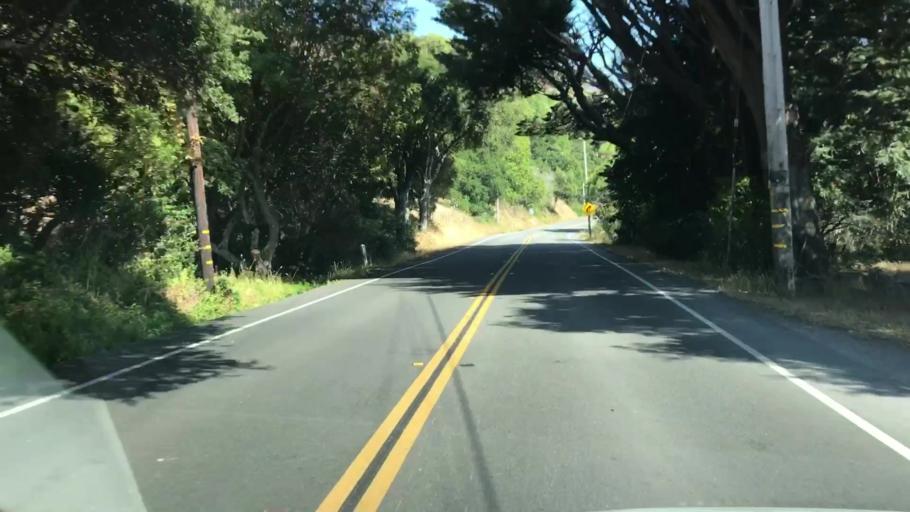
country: US
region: California
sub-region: Marin County
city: Lagunitas-Forest Knolls
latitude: 38.0439
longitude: -122.7465
